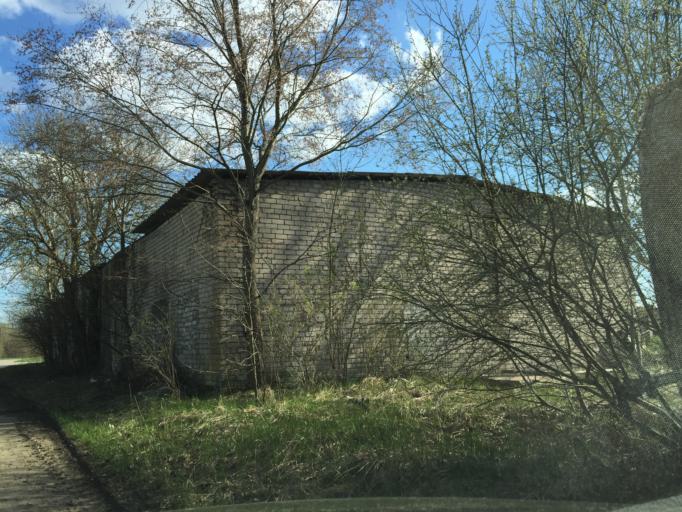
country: LV
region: Saulkrastu
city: Saulkrasti
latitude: 57.3314
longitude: 24.4926
